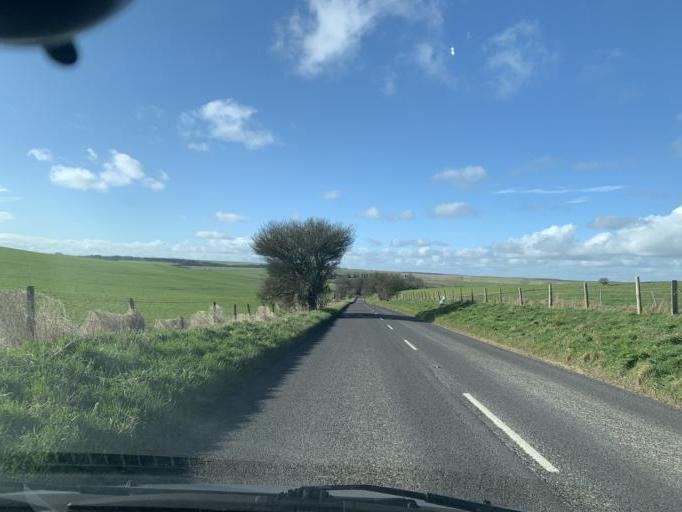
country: GB
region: England
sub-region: Wiltshire
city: Stockton
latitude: 51.1898
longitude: -2.0024
